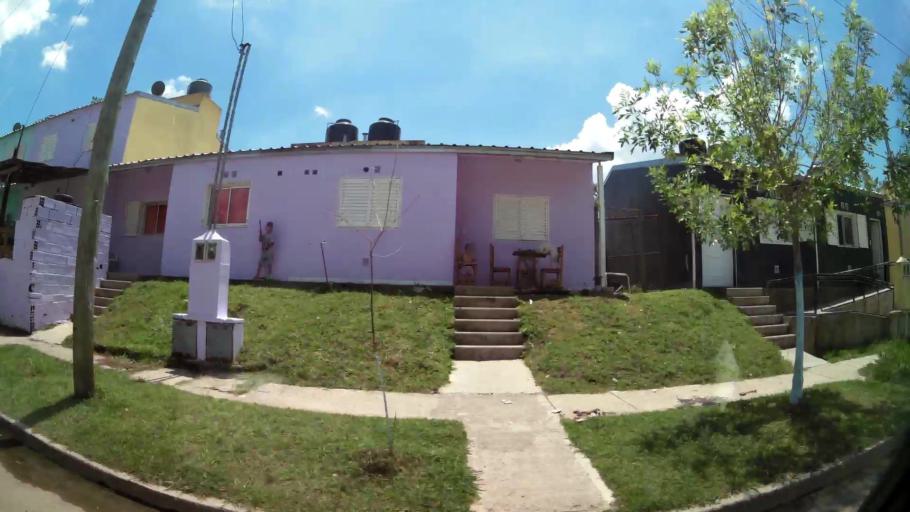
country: AR
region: Buenos Aires
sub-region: Partido de Tigre
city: Tigre
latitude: -34.4051
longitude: -58.6061
